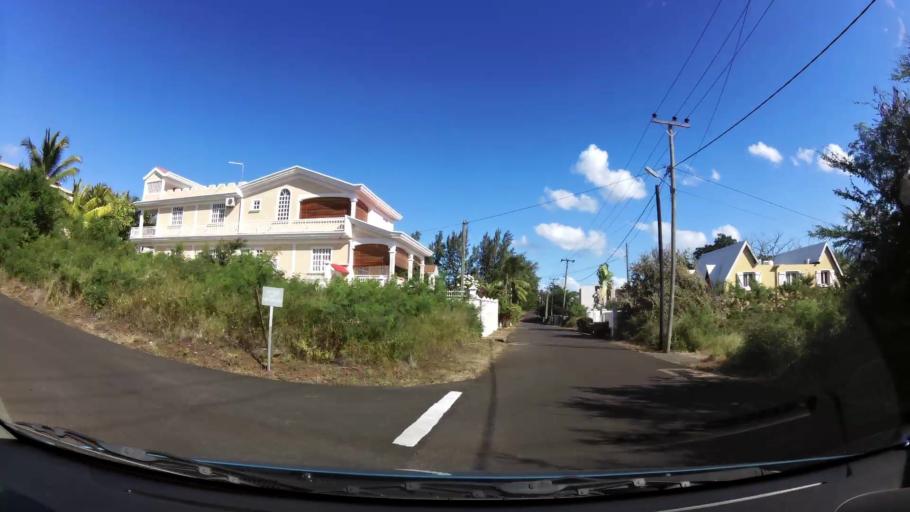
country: MU
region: Black River
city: Albion
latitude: -20.2168
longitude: 57.4068
